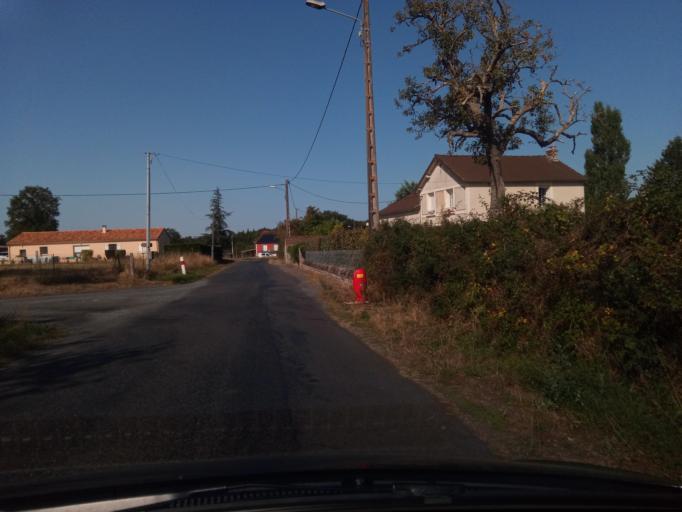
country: FR
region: Poitou-Charentes
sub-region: Departement de la Vienne
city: Saulge
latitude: 46.3298
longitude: 0.8366
